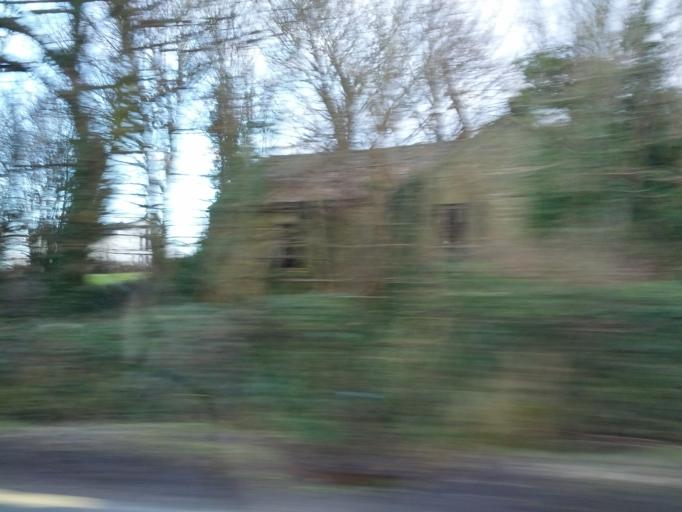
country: IE
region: Connaught
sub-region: County Galway
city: Tuam
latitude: 53.4391
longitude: -8.7304
